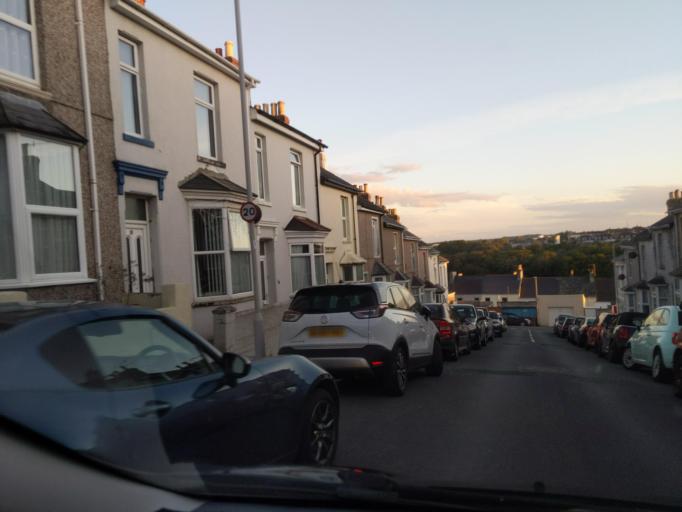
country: GB
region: England
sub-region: Plymouth
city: Plymstock
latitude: 50.3843
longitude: -4.1111
